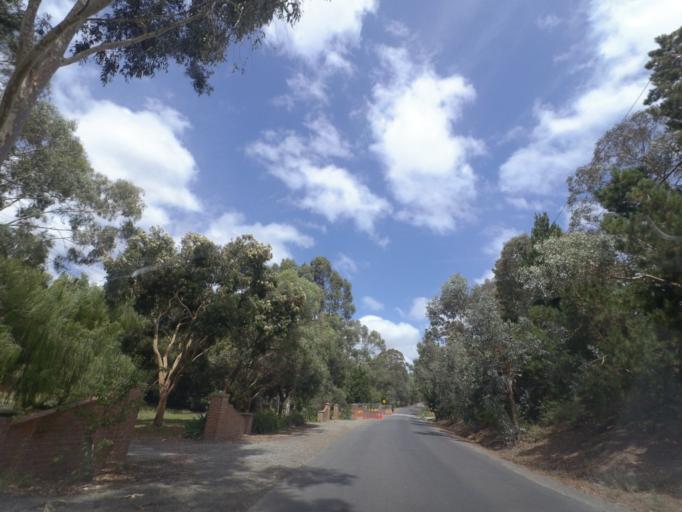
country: AU
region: Victoria
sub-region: Manningham
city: Park Orchards
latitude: -37.7964
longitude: 145.2106
